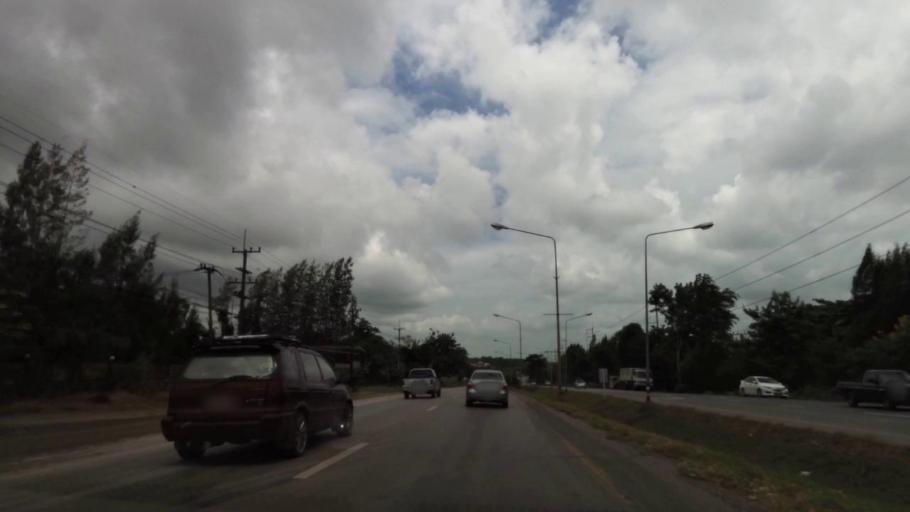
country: TH
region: Chanthaburi
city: Na Yai Am
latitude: 12.7827
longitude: 101.8017
